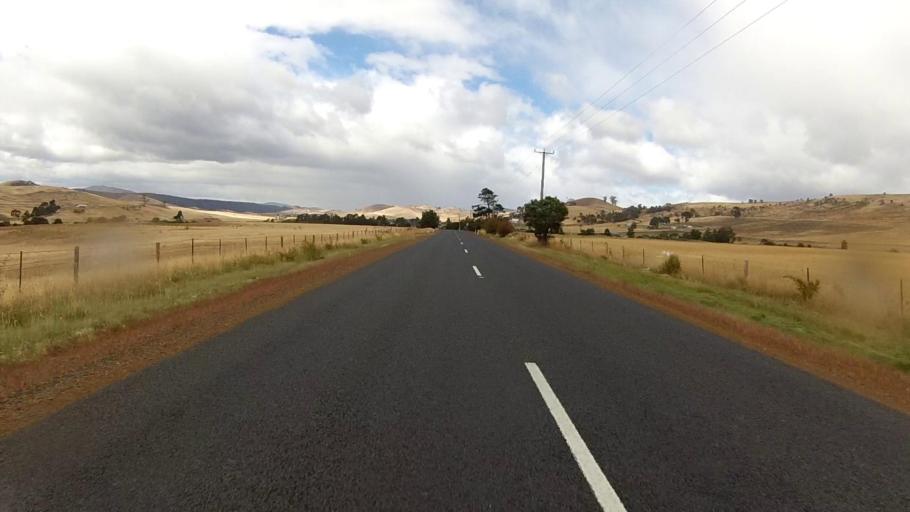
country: AU
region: Tasmania
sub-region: Brighton
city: Bridgewater
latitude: -42.5269
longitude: 147.3590
